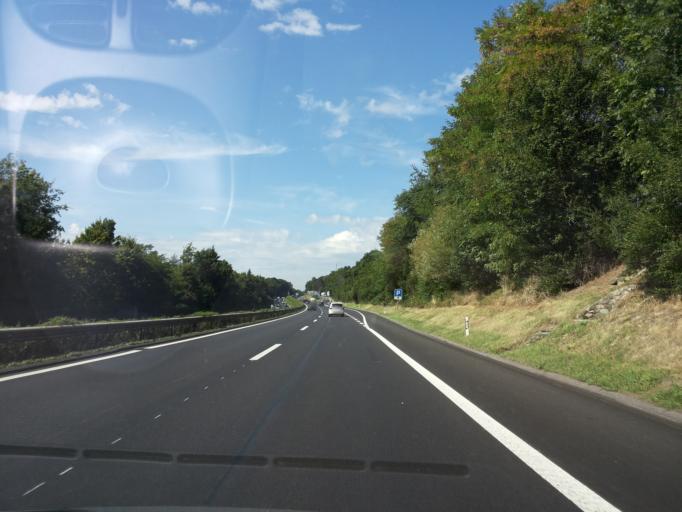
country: CH
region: Lucerne
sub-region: Sursee District
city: Sempach
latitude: 47.1419
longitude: 8.1901
